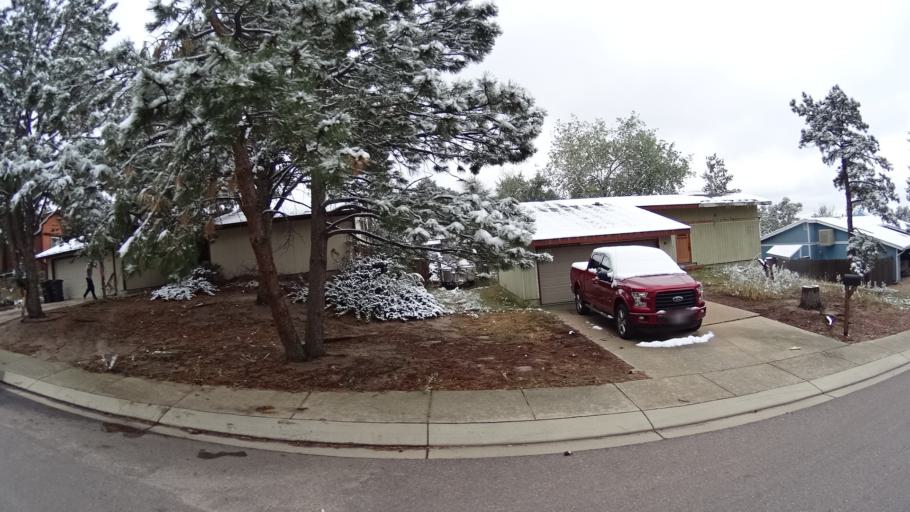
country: US
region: Colorado
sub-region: El Paso County
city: Cimarron Hills
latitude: 38.9193
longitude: -104.7734
